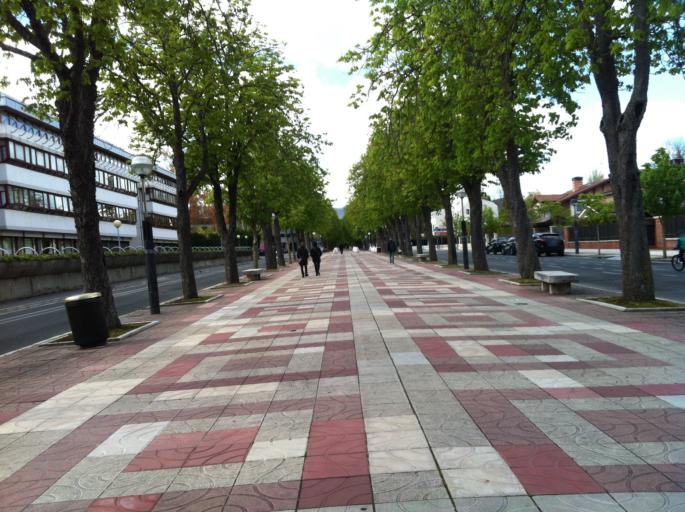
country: ES
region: Basque Country
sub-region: Provincia de Alava
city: Gasteiz / Vitoria
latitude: 42.8394
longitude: -2.6873
